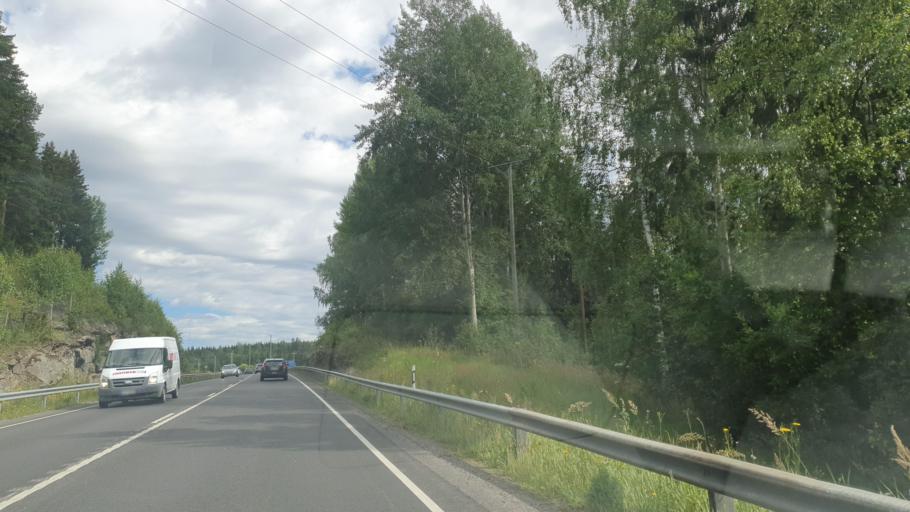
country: FI
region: Central Finland
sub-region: Jyvaeskylae
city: Korpilahti
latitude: 61.9920
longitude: 25.4596
